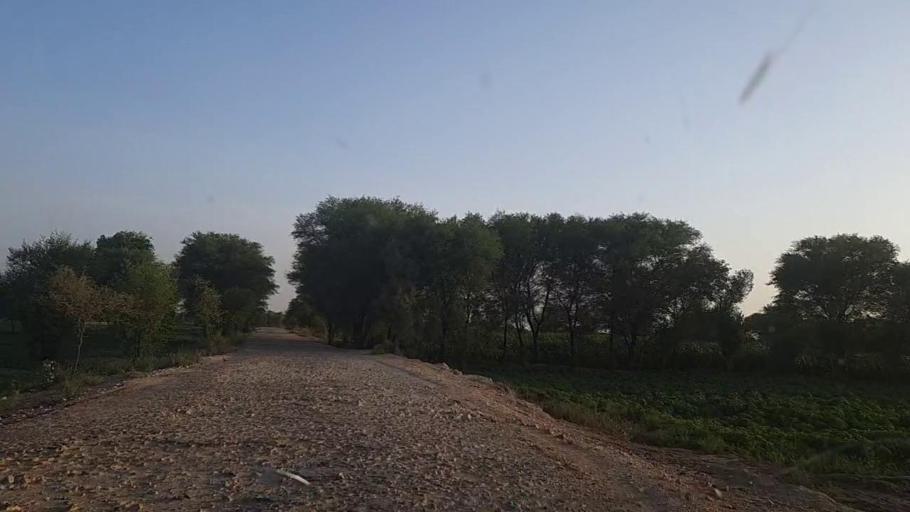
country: PK
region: Sindh
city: Khanpur
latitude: 27.6352
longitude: 69.4482
